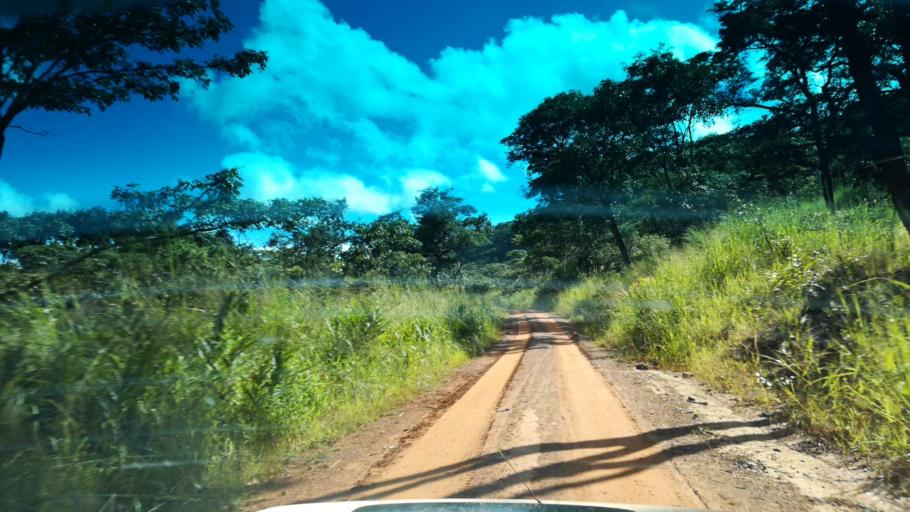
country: ZM
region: Northern
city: Kaputa
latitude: -7.9083
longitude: 29.1690
